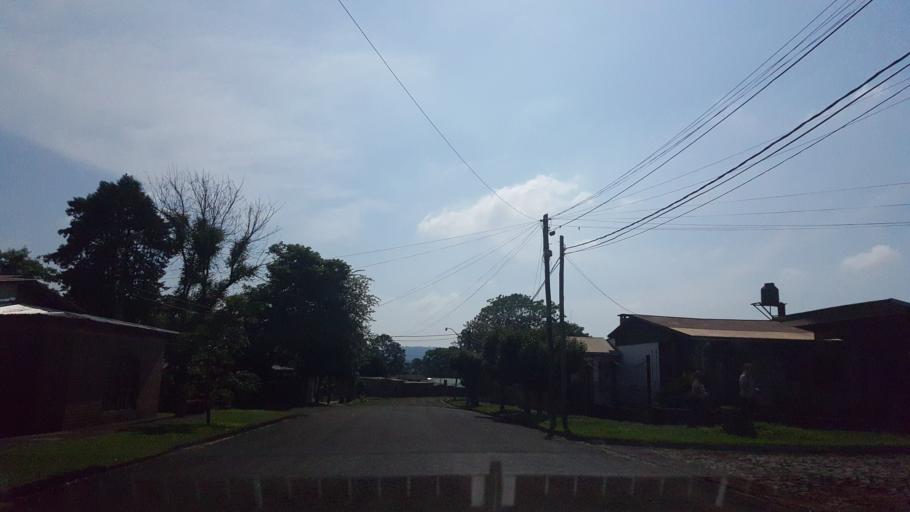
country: AR
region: Misiones
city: Capiovi
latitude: -26.9302
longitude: -55.0567
